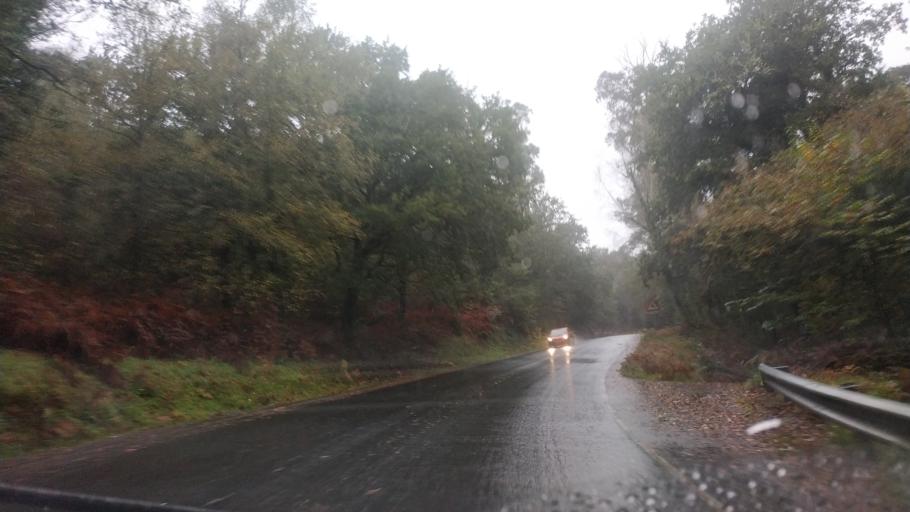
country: ES
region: Galicia
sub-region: Provincia da Coruna
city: Negreira
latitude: 42.9069
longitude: -8.7466
